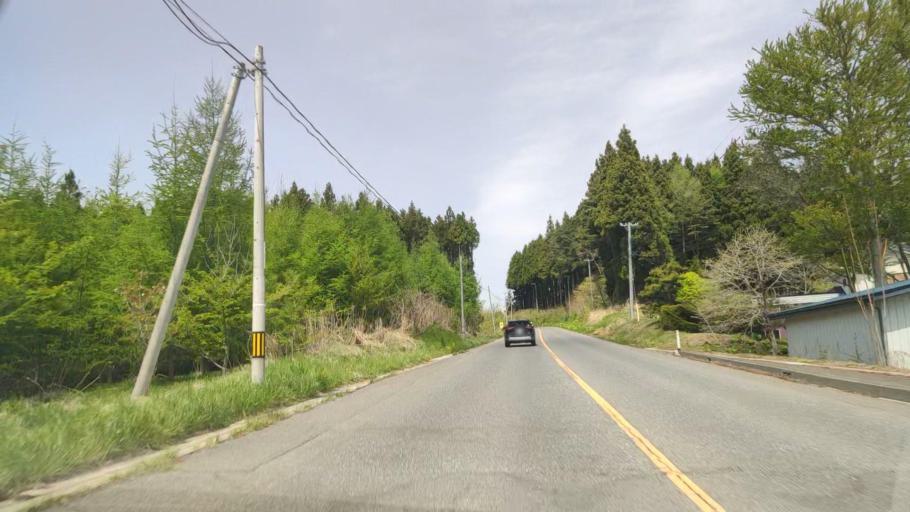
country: JP
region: Aomori
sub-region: Misawa Shi
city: Inuotose
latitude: 40.5642
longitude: 141.3814
